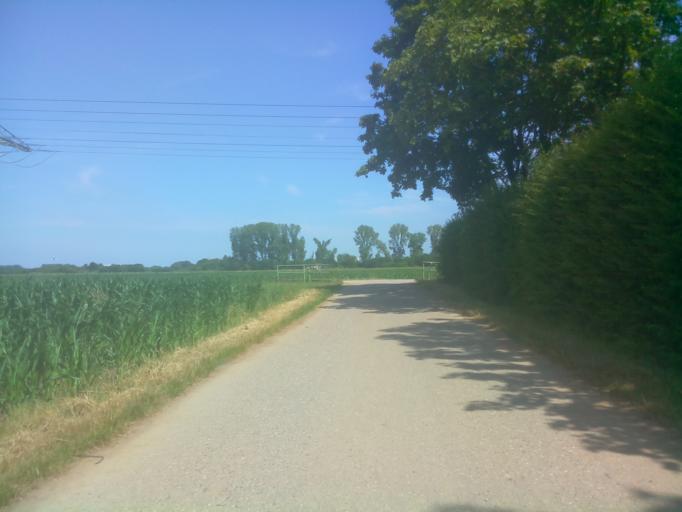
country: DE
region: Baden-Wuerttemberg
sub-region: Karlsruhe Region
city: Laudenbach
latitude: 49.6125
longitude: 8.6332
